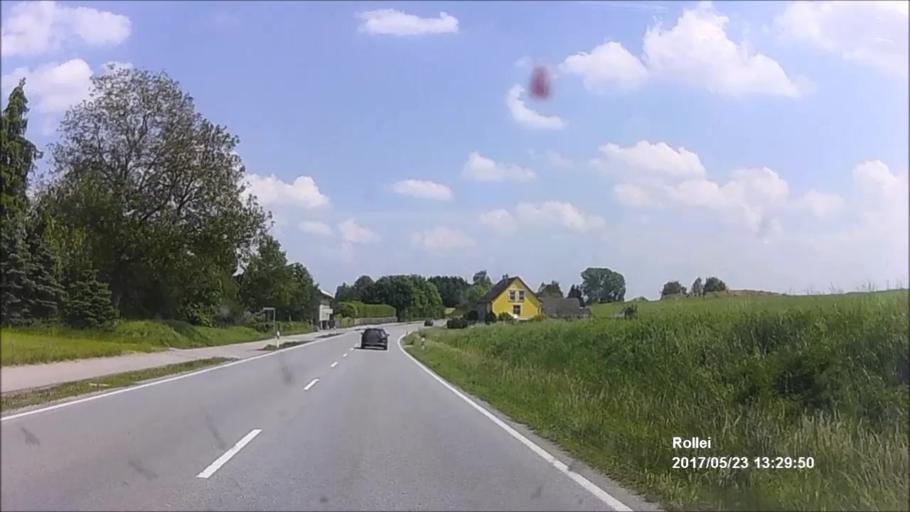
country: DE
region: Bavaria
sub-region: Upper Bavaria
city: Dorfen
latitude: 48.2843
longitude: 12.1366
